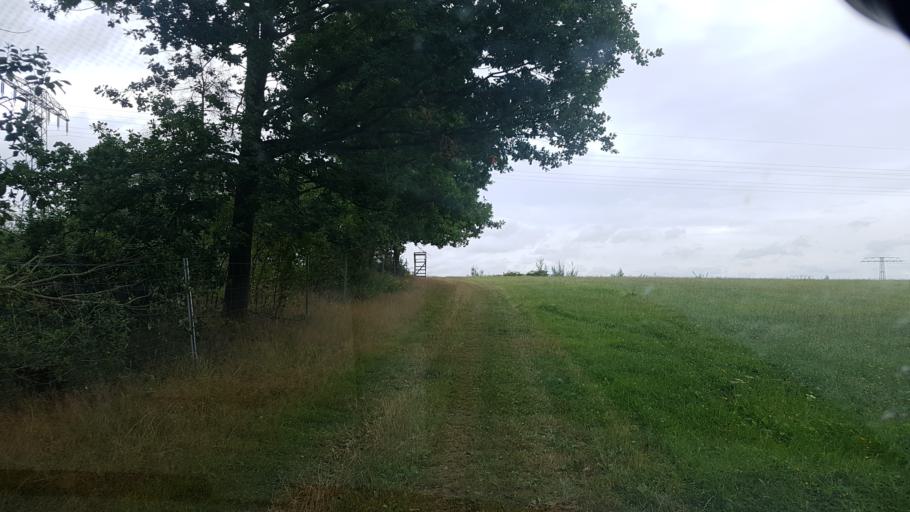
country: DE
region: Saxony
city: Grossrohrsdorf
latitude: 51.1580
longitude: 14.0389
